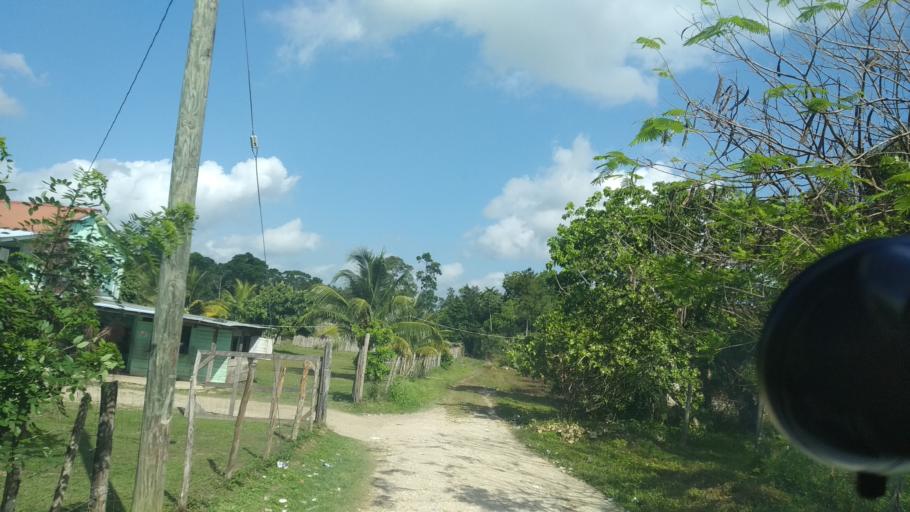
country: BZ
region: Stann Creek
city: Placencia
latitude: 16.4741
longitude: -88.6235
